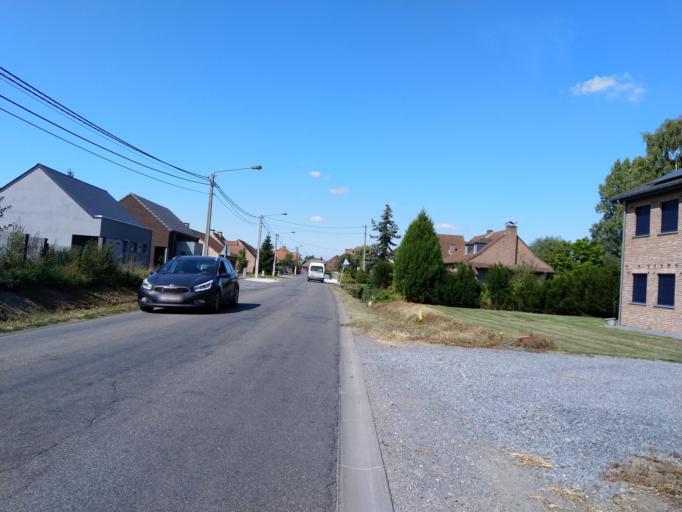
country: BE
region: Wallonia
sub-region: Province du Hainaut
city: Jurbise
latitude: 50.5249
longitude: 3.8612
